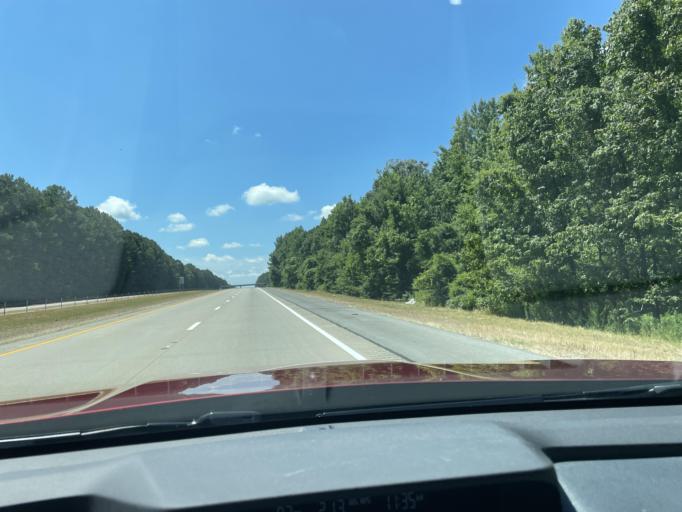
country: US
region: Arkansas
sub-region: Jefferson County
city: Redfield
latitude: 34.4463
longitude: -92.1992
